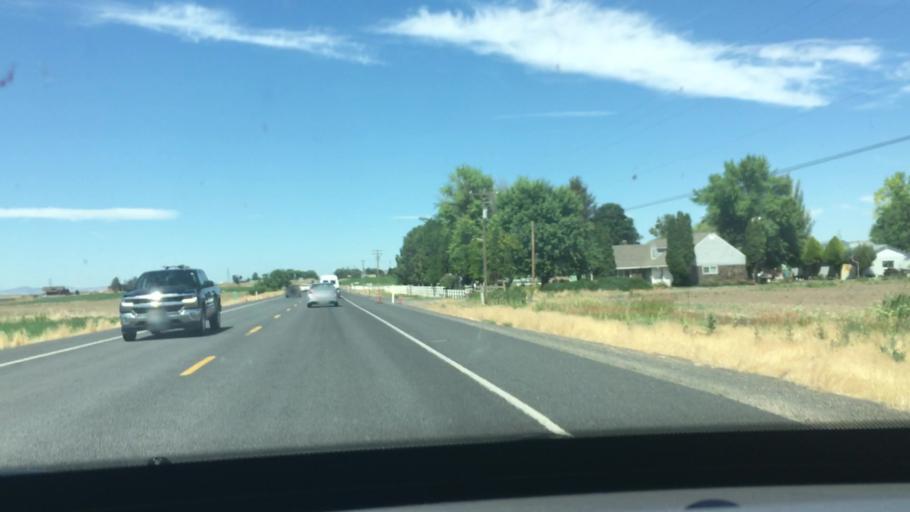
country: US
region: Oregon
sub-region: Jefferson County
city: Culver
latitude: 44.5558
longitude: -121.1664
